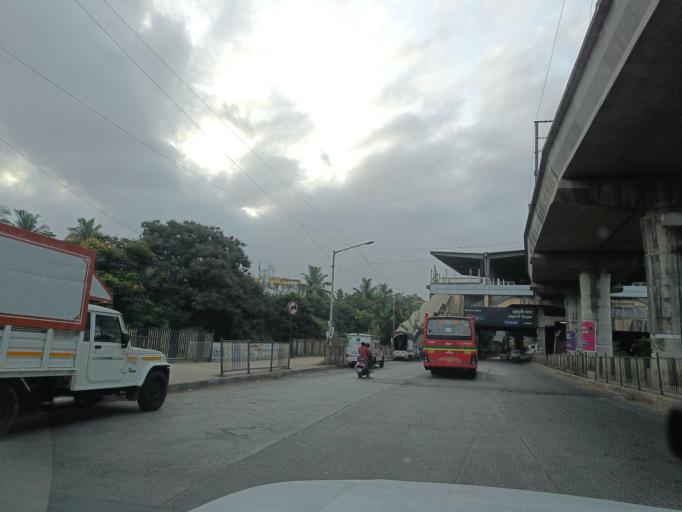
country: IN
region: Maharashtra
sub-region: Mumbai Suburban
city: Powai
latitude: 19.0933
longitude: 72.9005
